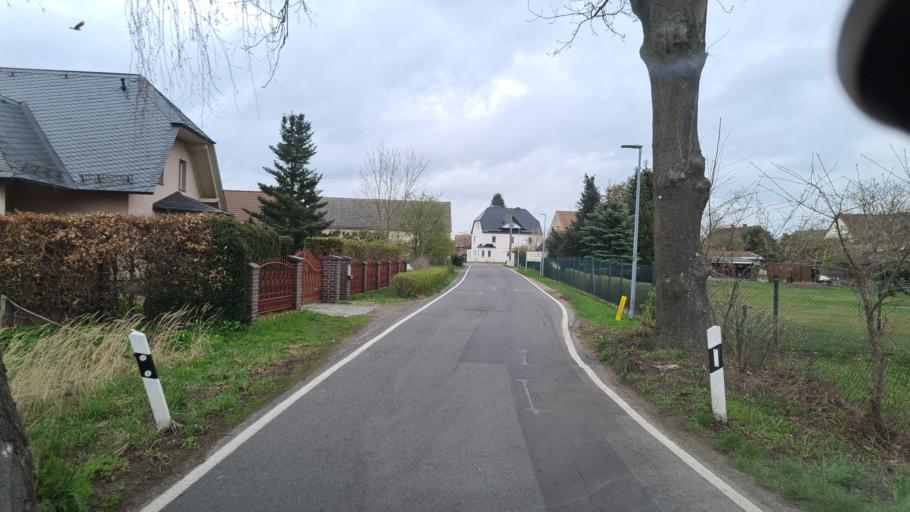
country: DE
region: Brandenburg
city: Schwarzbach
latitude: 51.4544
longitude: 13.9325
